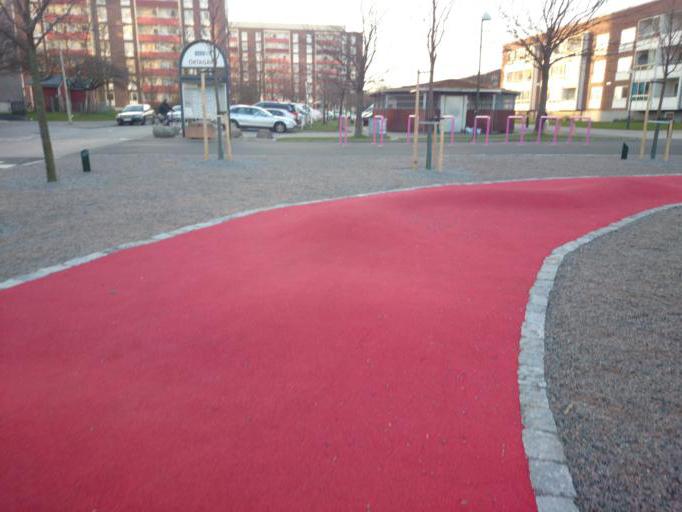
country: SE
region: Skane
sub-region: Malmo
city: Malmoe
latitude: 55.5854
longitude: 13.0420
